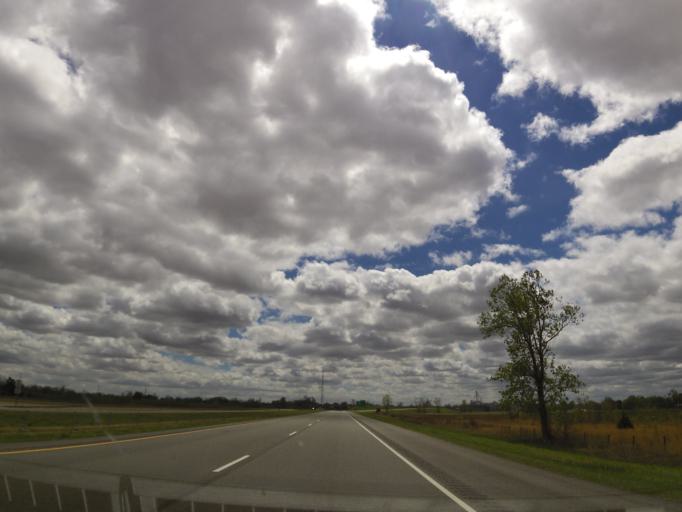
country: US
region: Arkansas
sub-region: Poinsett County
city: Marked Tree
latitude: 35.5532
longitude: -90.4970
